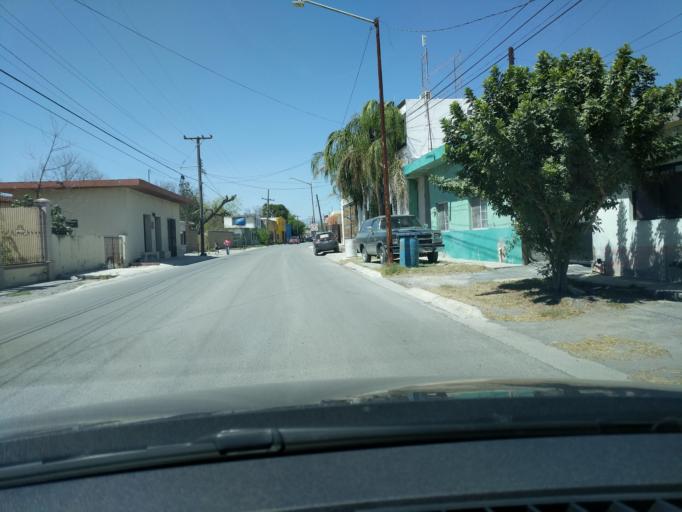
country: MX
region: Nuevo Leon
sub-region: Apodaca
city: Artemio Trevino
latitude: 25.8121
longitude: -100.1453
